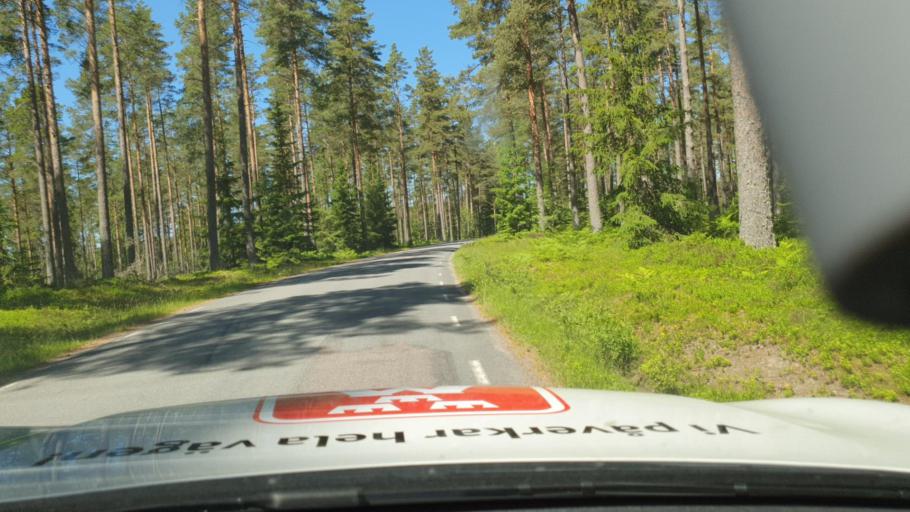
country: SE
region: Joenkoeping
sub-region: Habo Kommun
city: Habo
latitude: 57.8896
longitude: 13.9982
